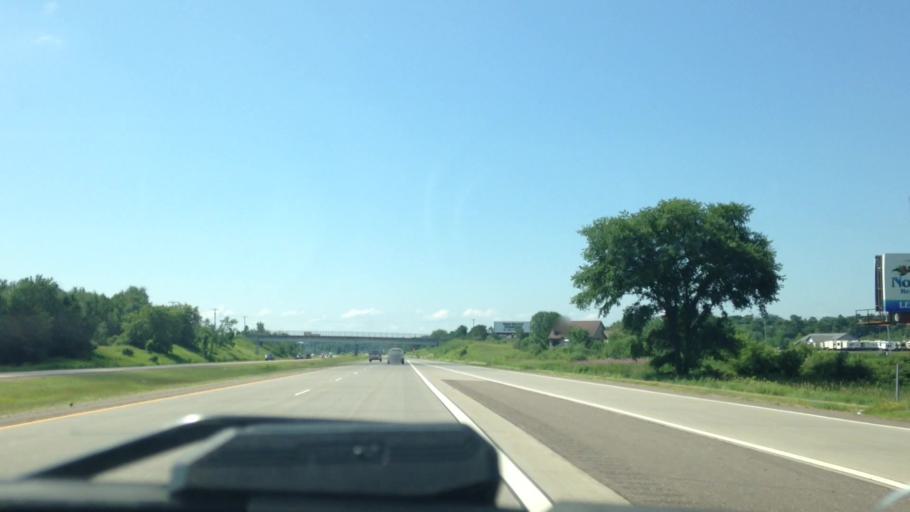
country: US
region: Wisconsin
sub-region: Barron County
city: Rice Lake
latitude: 45.5058
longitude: -91.7631
